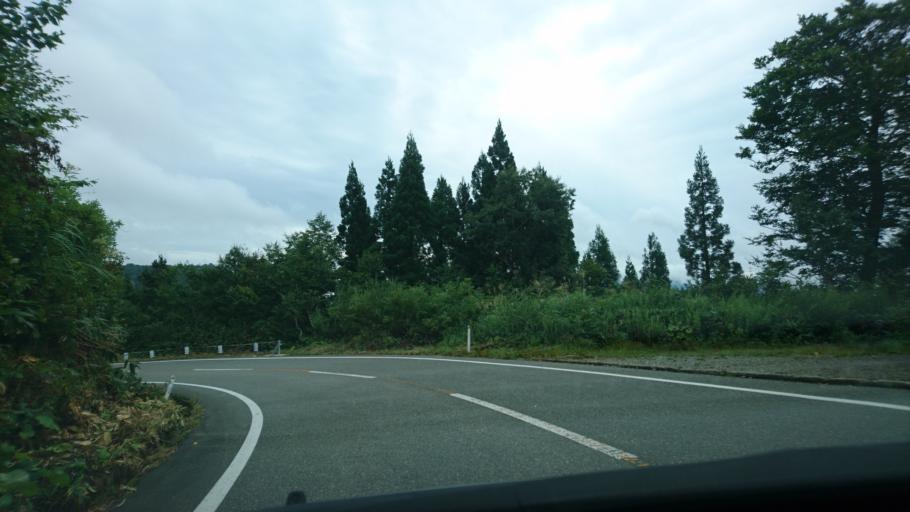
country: JP
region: Akita
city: Yuzawa
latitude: 38.9787
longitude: 140.7201
